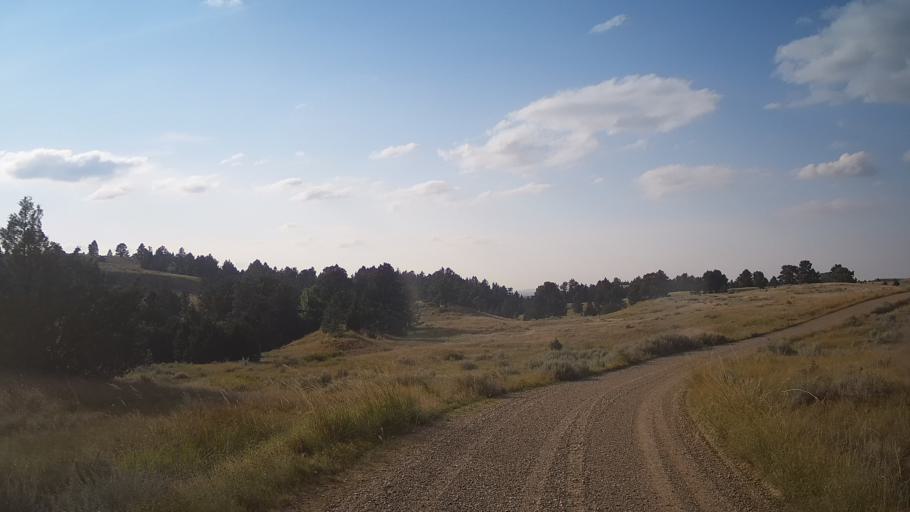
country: US
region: Montana
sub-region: Dawson County
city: Glendive
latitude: 47.0555
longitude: -104.6719
